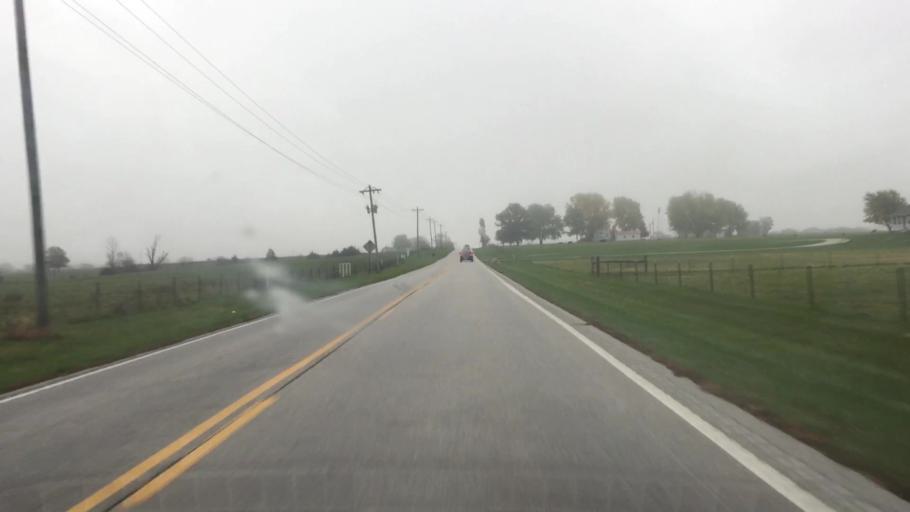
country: US
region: Missouri
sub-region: Callaway County
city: Fulton
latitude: 38.8739
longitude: -92.0647
